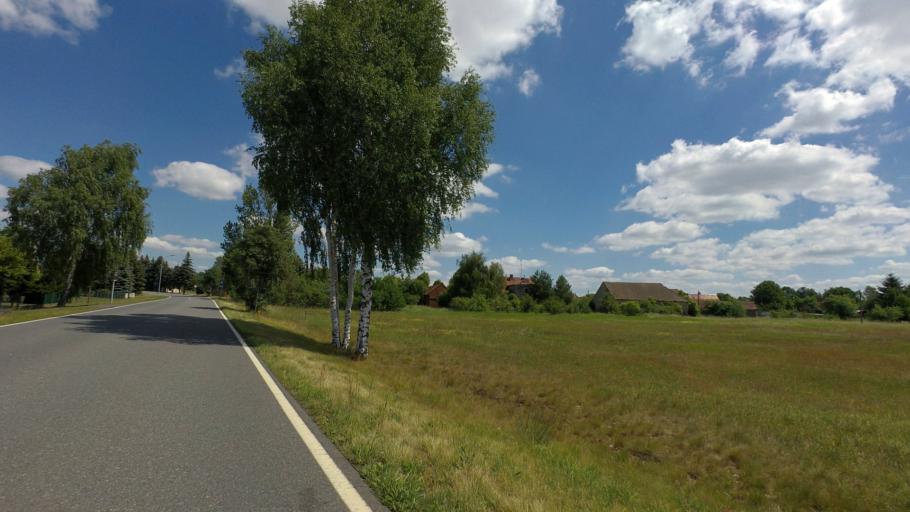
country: DE
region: Brandenburg
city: Luckau
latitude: 51.7723
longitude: 13.6874
